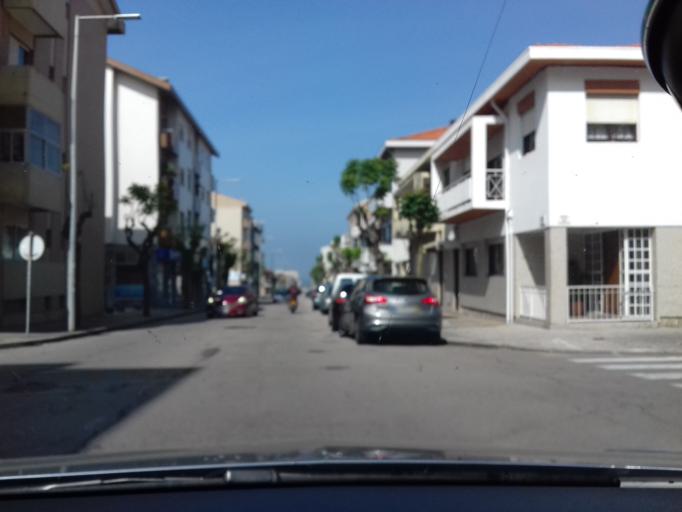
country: PT
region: Aveiro
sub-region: Espinho
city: Espinho
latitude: 41.0040
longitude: -8.6352
